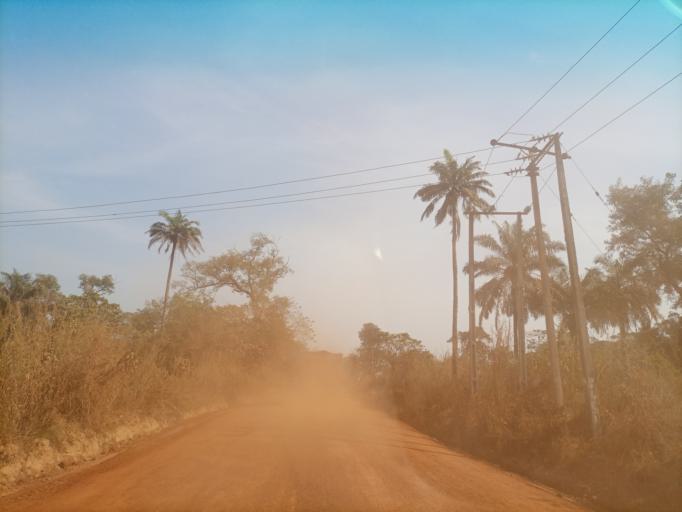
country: NG
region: Enugu
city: Eha Amufu
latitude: 6.6663
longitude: 7.7541
